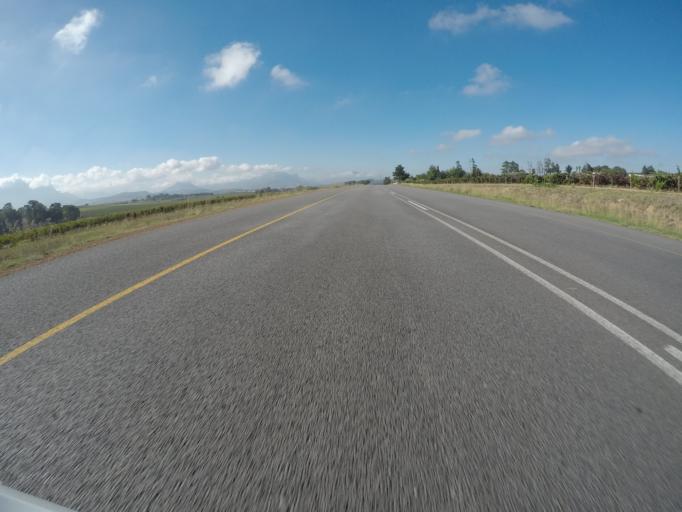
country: ZA
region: Western Cape
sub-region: Cape Winelands District Municipality
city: Stellenbosch
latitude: -33.8608
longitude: 18.8108
